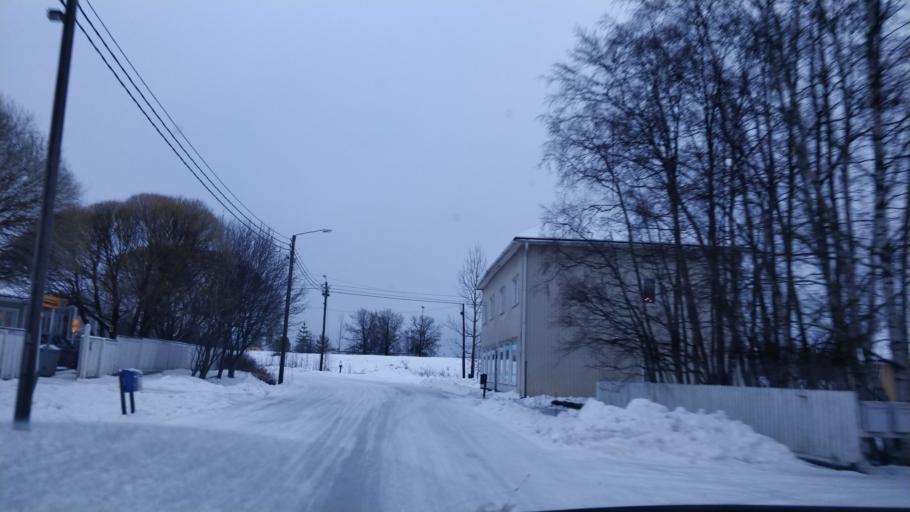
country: FI
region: Lapland
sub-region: Kemi-Tornio
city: Kemi
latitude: 65.7459
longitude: 24.5774
